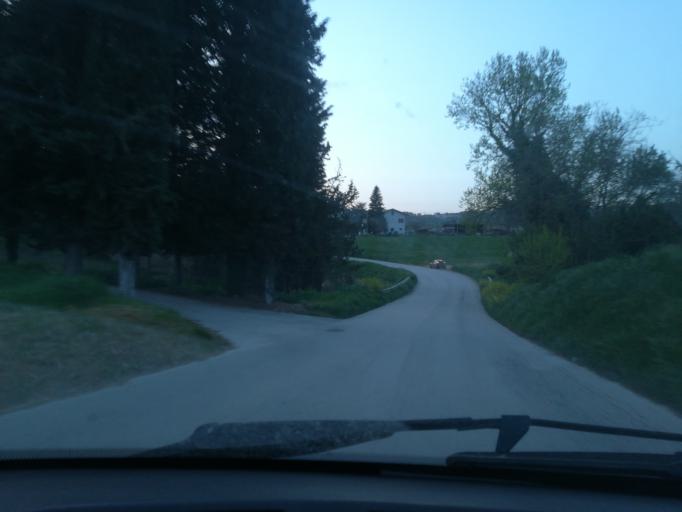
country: IT
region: The Marches
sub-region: Provincia di Macerata
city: Piediripa
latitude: 43.2696
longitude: 13.4619
